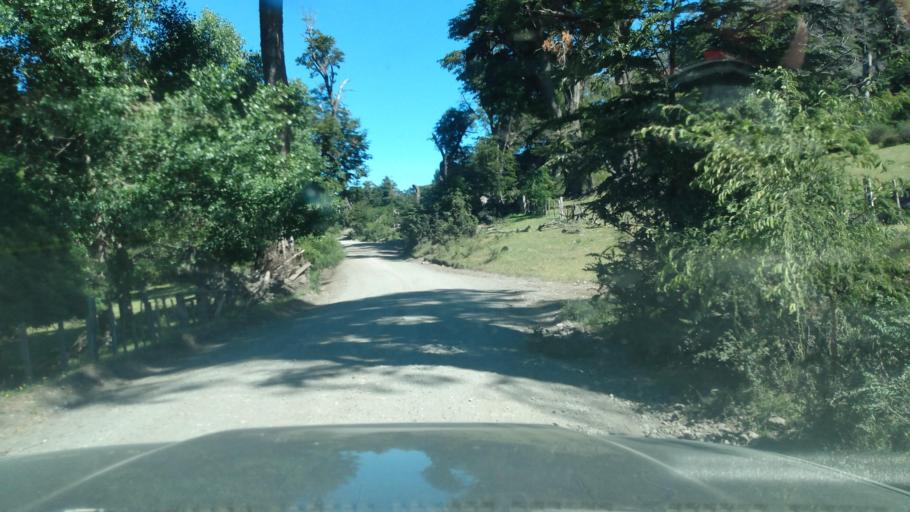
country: AR
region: Neuquen
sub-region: Departamento de Lacar
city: San Martin de los Andes
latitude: -39.7527
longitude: -71.4536
